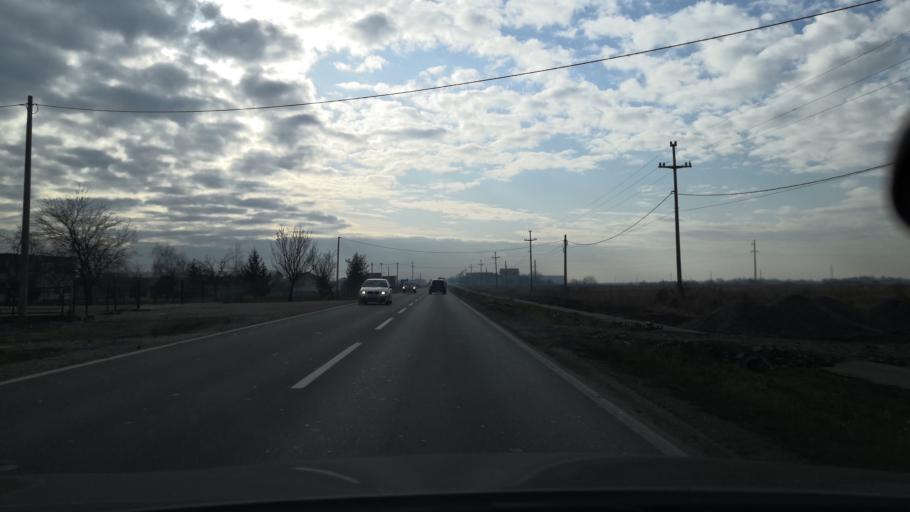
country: RS
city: Ugrinovci
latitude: 44.8652
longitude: 20.2045
